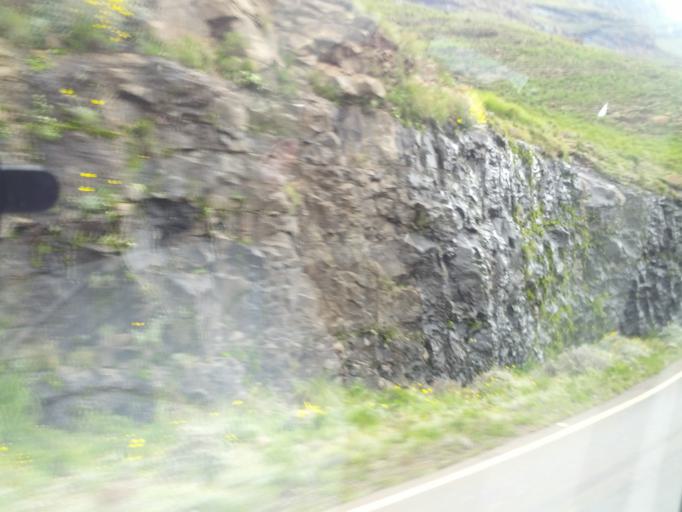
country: LS
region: Butha-Buthe
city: Butha-Buthe
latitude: -29.0719
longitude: 28.3772
